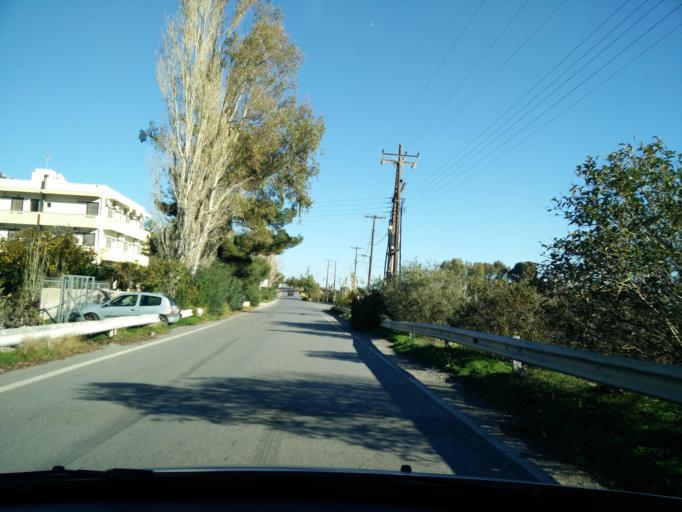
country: GR
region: Crete
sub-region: Nomos Lasithiou
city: Gra Liyia
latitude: 35.0053
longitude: 25.5855
